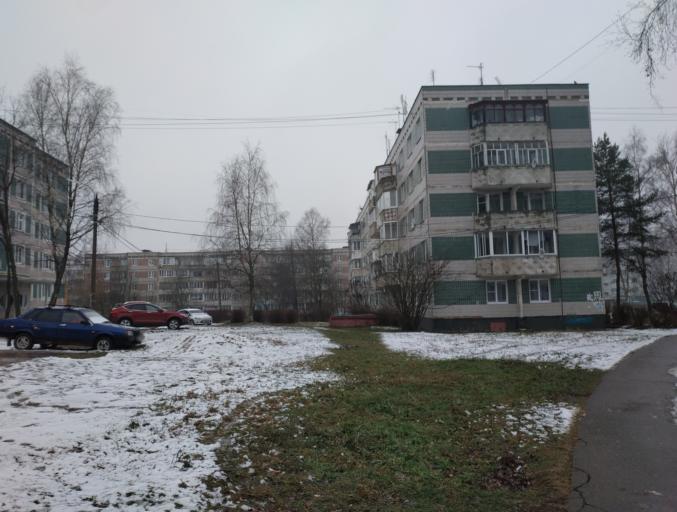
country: RU
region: Moskovskaya
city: Taldom
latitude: 56.7426
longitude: 37.5314
